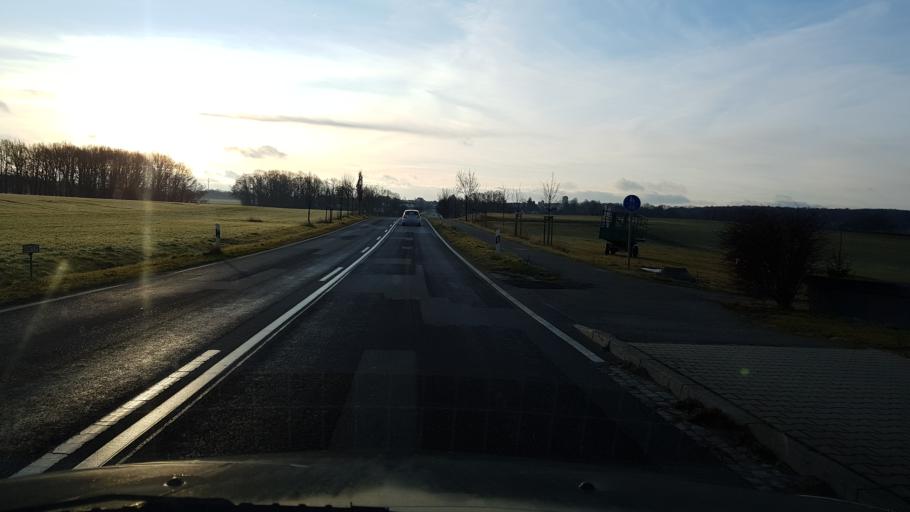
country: DE
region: Saxony
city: Radibor
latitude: 51.2209
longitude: 14.3891
